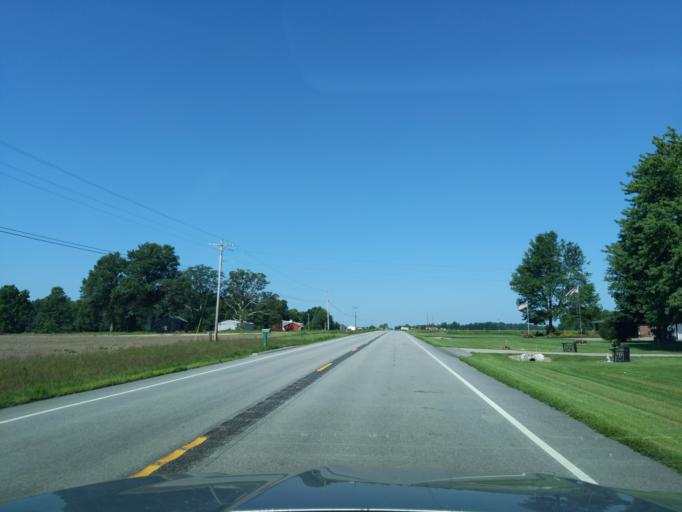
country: US
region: Indiana
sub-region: Ripley County
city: Versailles
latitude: 39.0750
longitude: -85.2788
